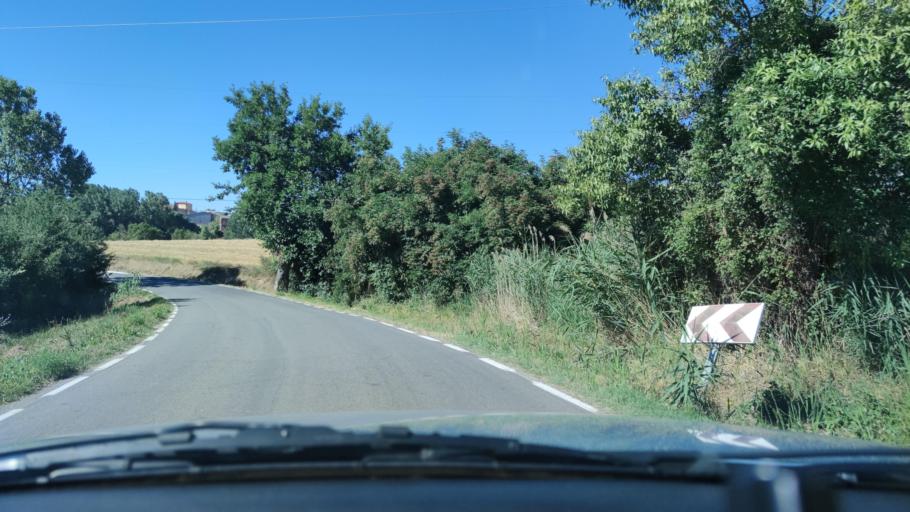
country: ES
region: Catalonia
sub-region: Provincia de Lleida
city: Solsona
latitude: 41.9875
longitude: 1.5065
